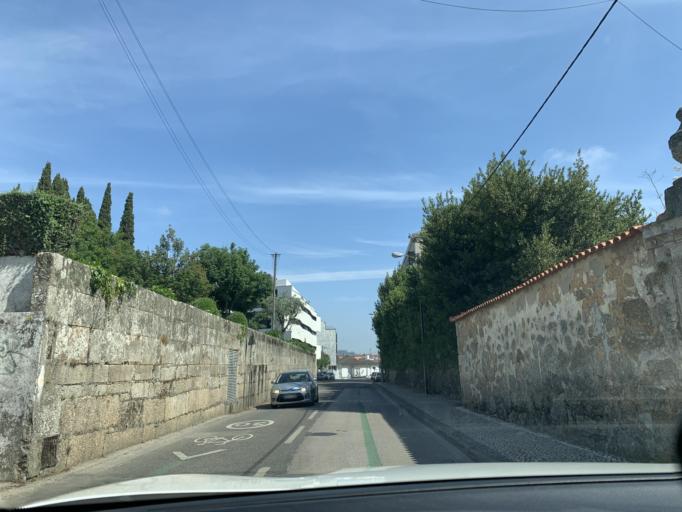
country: PT
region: Viseu
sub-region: Viseu
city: Viseu
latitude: 40.6542
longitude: -7.9116
